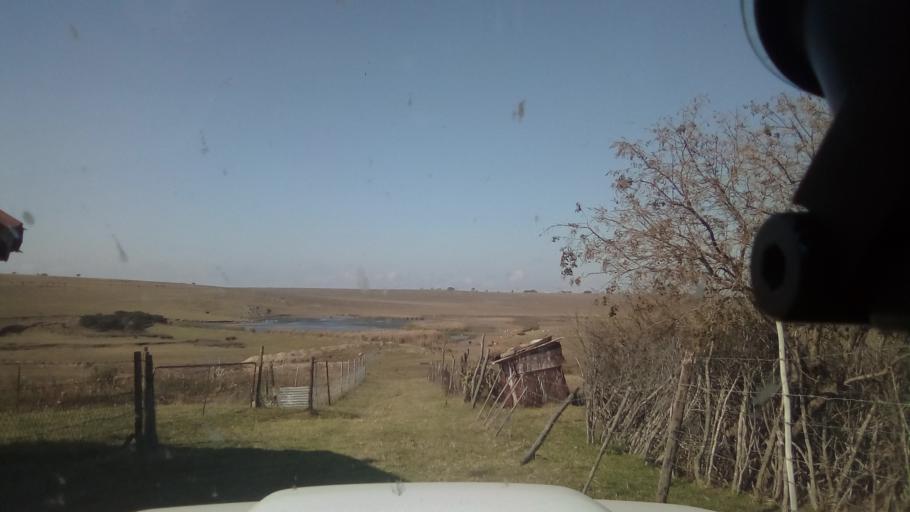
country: ZA
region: Eastern Cape
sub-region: Buffalo City Metropolitan Municipality
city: Bhisho
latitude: -32.9478
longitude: 27.3250
